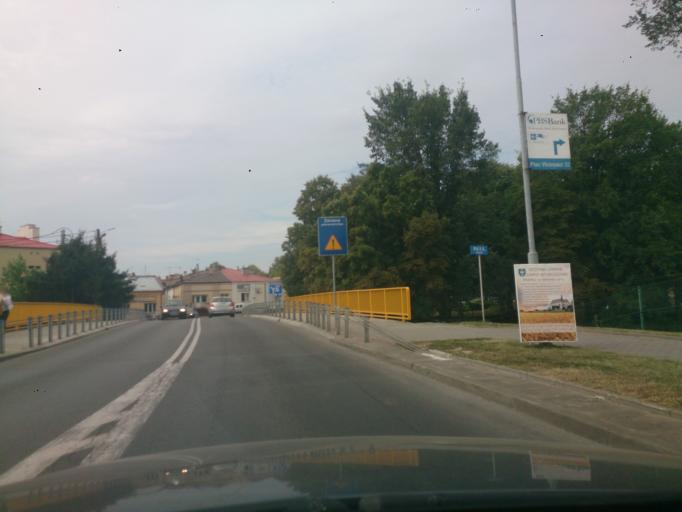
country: PL
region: Subcarpathian Voivodeship
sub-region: Powiat kolbuszowski
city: Kolbuszowa
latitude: 50.2441
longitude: 21.7779
